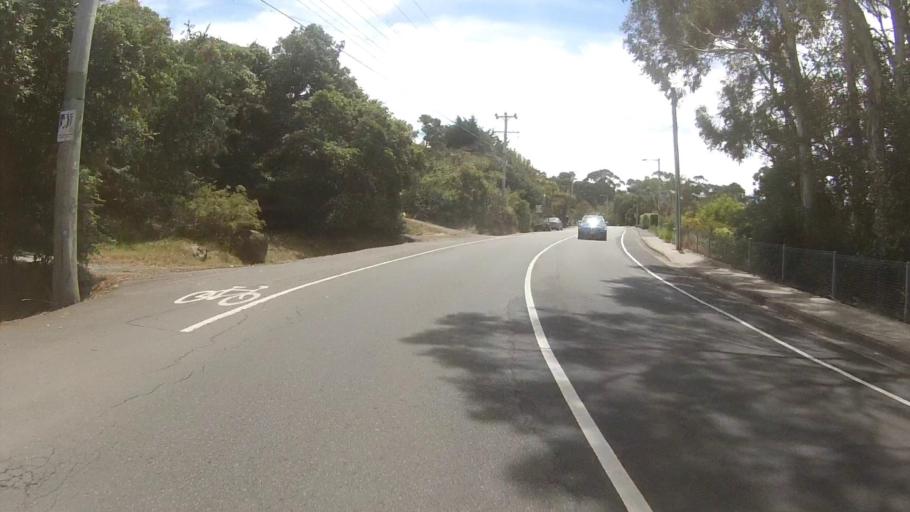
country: AU
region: Tasmania
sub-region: Kingborough
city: Taroona
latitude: -42.9396
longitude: 147.3529
